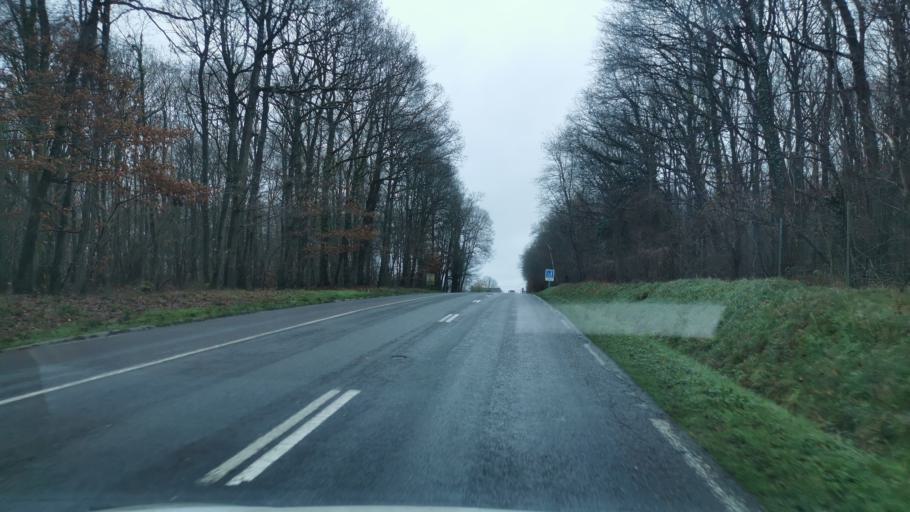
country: FR
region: Haute-Normandie
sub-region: Departement de l'Eure
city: Normanville
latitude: 49.0762
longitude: 1.1779
